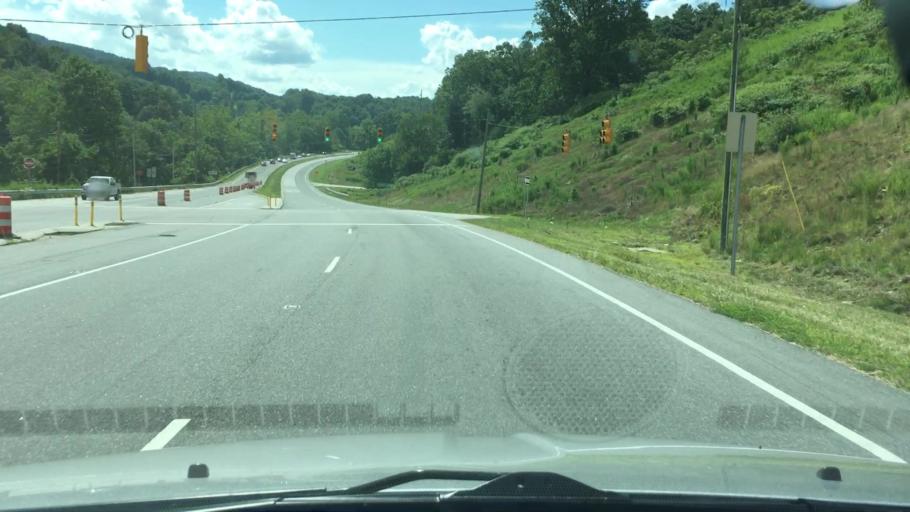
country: US
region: North Carolina
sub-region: Yancey County
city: Burnsville
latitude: 35.9110
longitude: -82.2229
